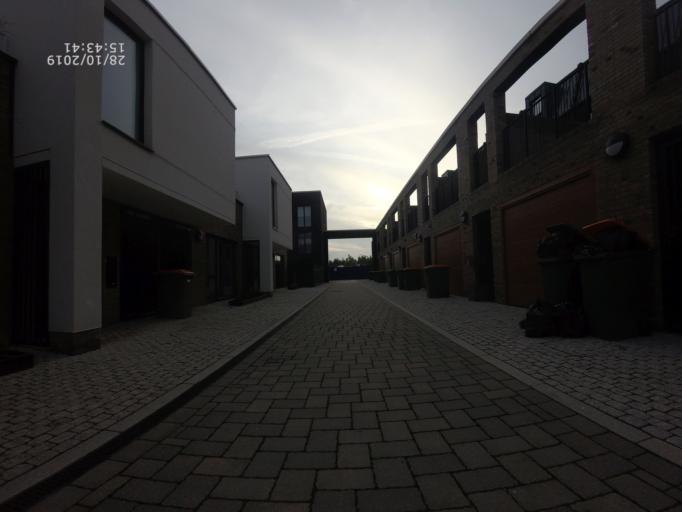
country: GB
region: England
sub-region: Greater London
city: Hackney
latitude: 51.5485
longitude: -0.0129
